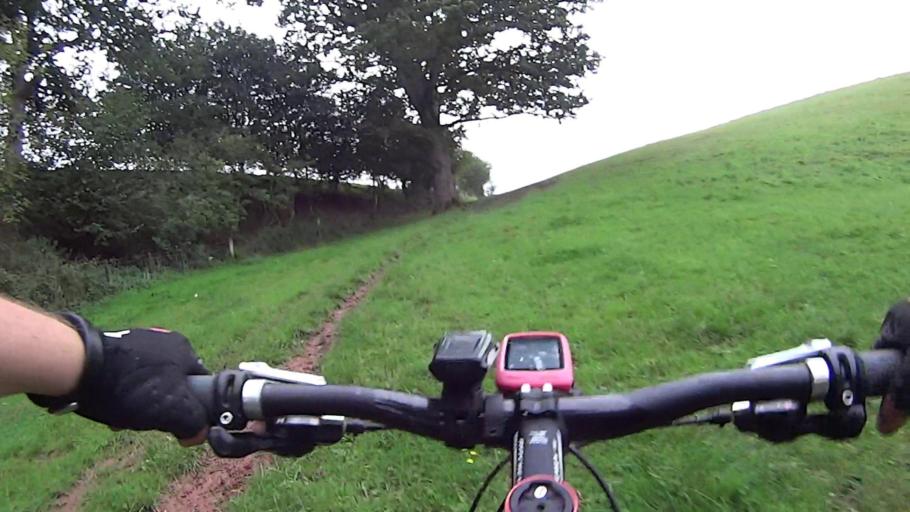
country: GB
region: England
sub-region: Worcestershire
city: Tenbury Wells
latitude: 52.2949
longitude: -2.5844
